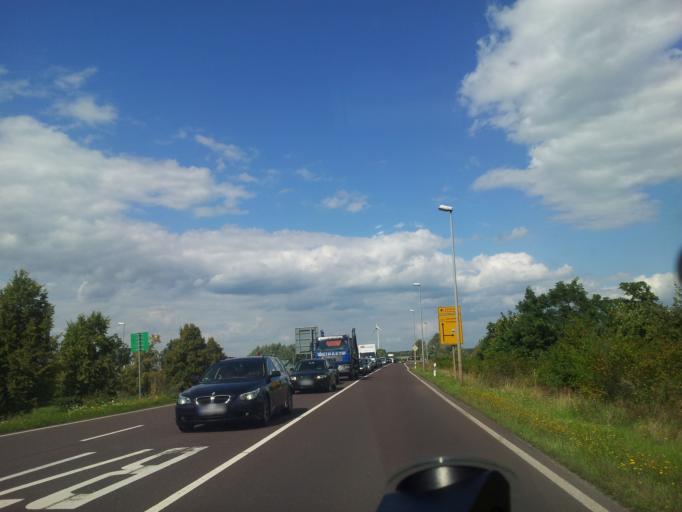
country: DE
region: Saxony-Anhalt
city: Haldensleben I
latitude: 52.2827
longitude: 11.4334
